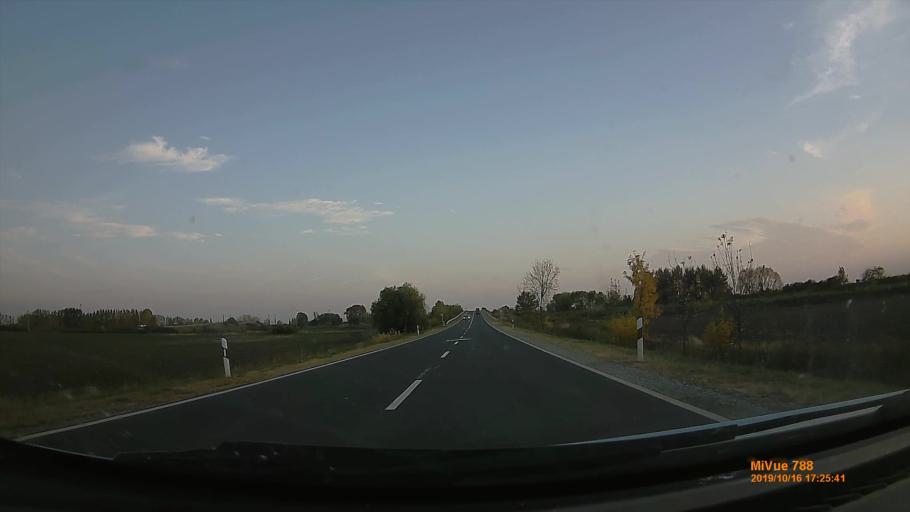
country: HU
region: Heves
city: Fuzesabony
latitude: 47.7537
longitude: 20.3959
